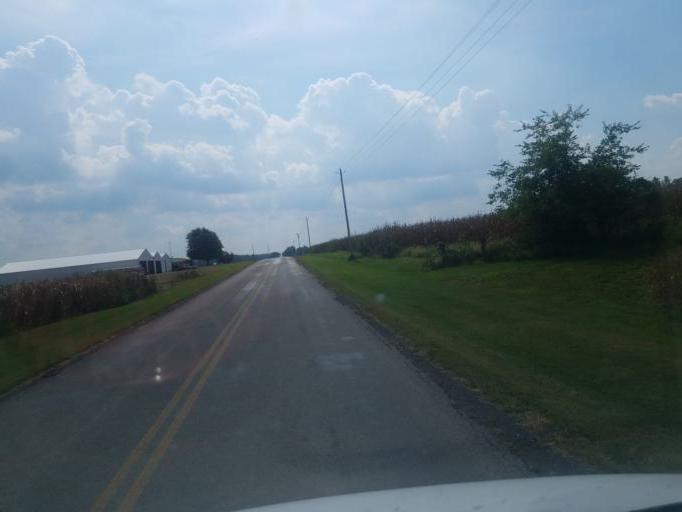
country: US
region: Ohio
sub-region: Logan County
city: Northwood
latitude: 40.6213
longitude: -83.7626
